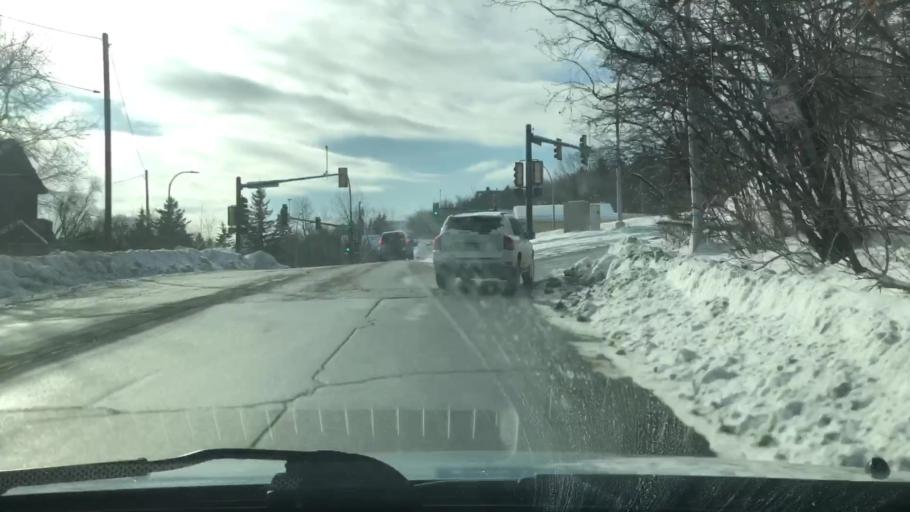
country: US
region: Minnesota
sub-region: Saint Louis County
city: Duluth
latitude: 46.7915
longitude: -92.1062
